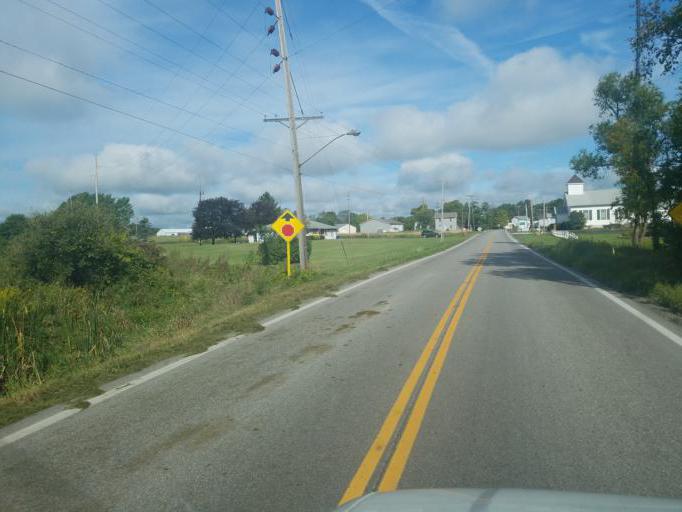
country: US
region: Ohio
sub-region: Wayne County
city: West Salem
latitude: 41.0247
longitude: -82.1241
